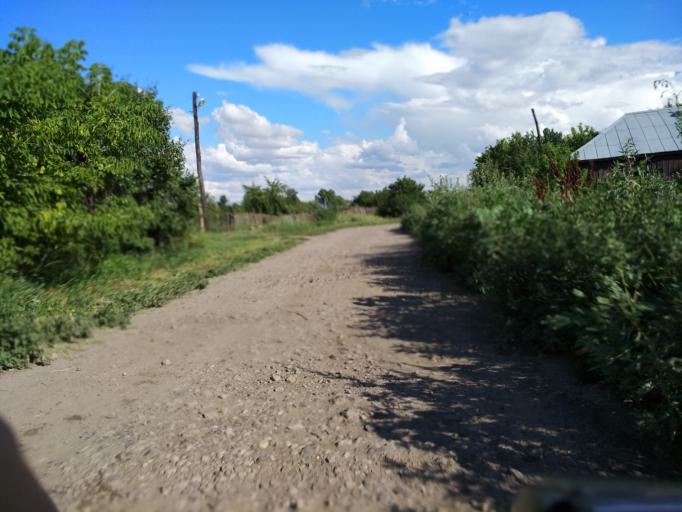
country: RU
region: Lipetsk
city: Dobrinka
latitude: 52.0333
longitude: 40.5623
